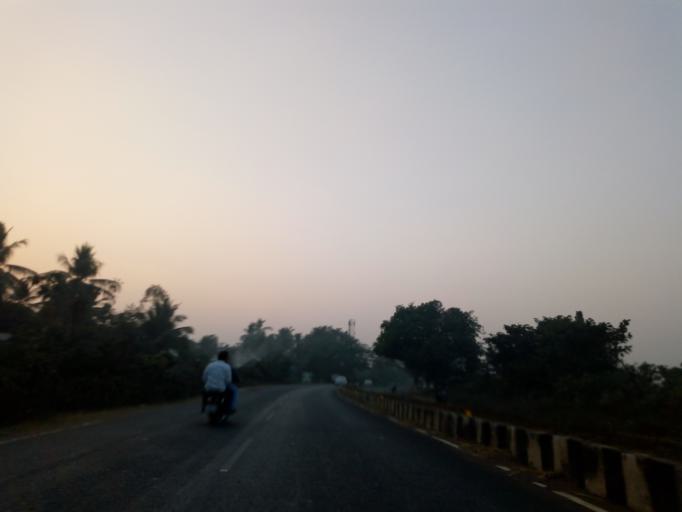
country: IN
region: Andhra Pradesh
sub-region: West Godavari
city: Tadepallegudem
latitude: 16.8109
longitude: 81.5129
